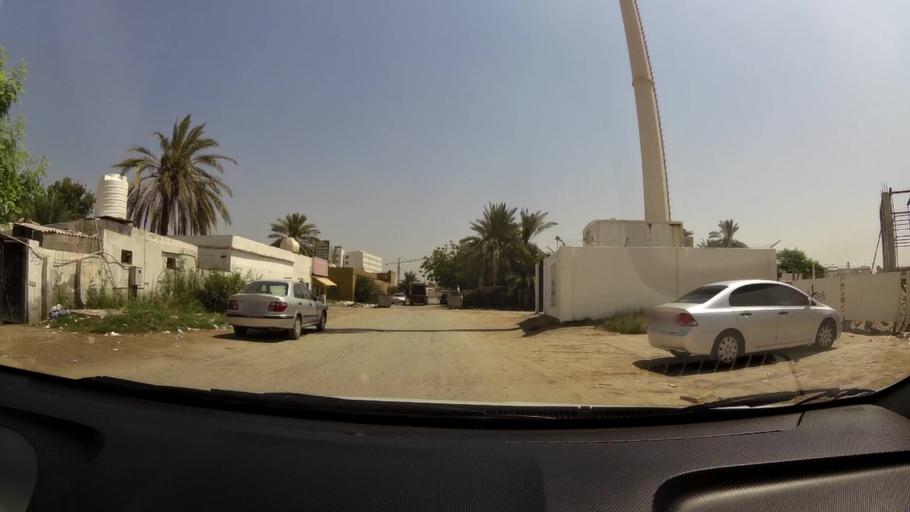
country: AE
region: Umm al Qaywayn
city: Umm al Qaywayn
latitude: 25.5641
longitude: 55.5542
